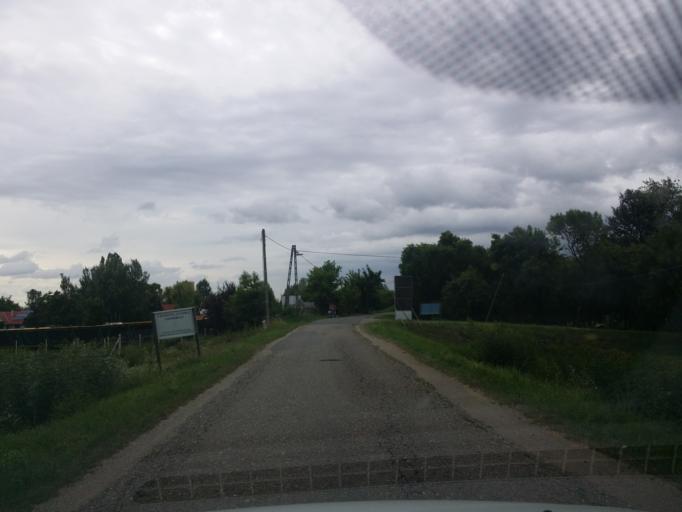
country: HU
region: Heves
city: Tiszanana
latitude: 47.5796
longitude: 20.6091
